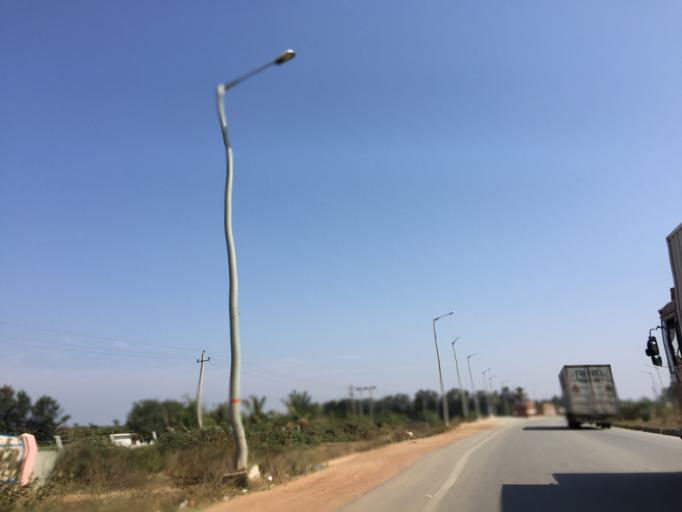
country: IN
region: Karnataka
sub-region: Bangalore Rural
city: Dasarahalli
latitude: 13.1121
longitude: 77.8801
